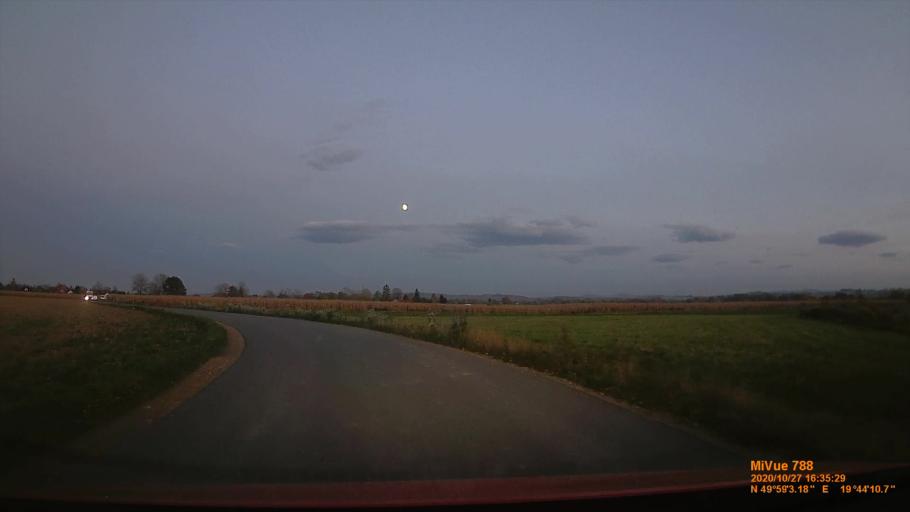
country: PL
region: Lesser Poland Voivodeship
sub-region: Powiat krakowski
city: Wolowice
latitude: 49.9843
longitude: 19.7364
